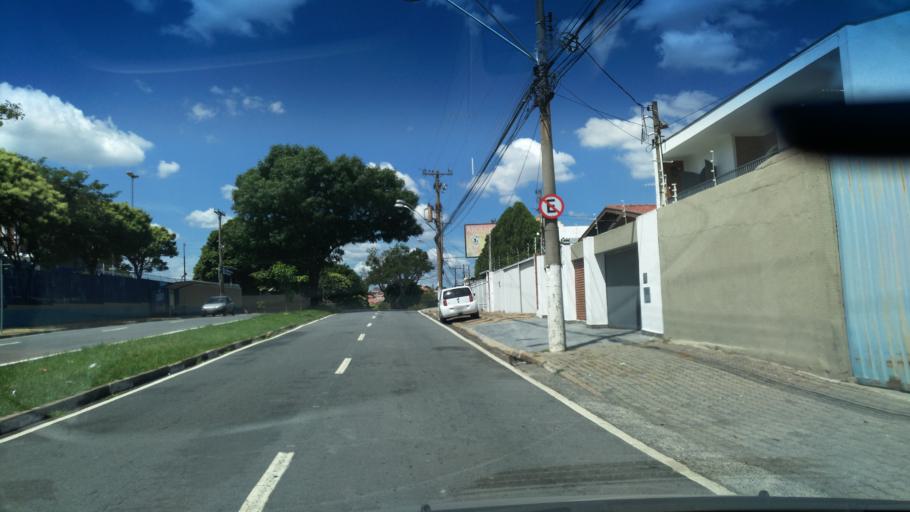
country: BR
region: Sao Paulo
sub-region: Campinas
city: Campinas
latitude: -22.9289
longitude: -47.0400
